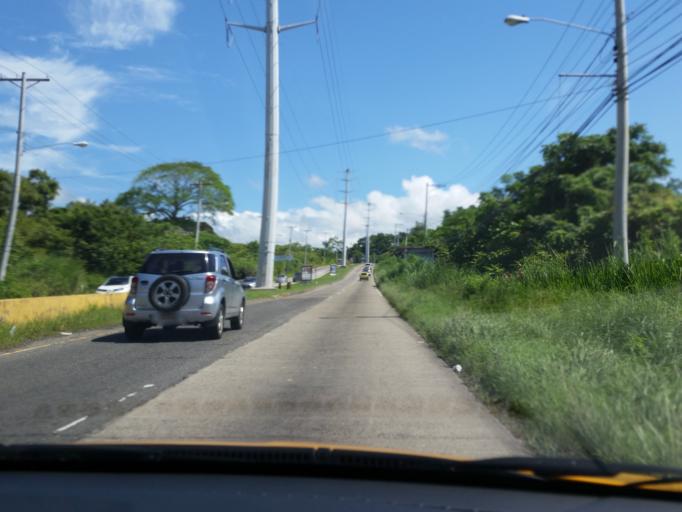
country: PA
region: Panama
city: San Miguelito
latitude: 9.0611
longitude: -79.4621
